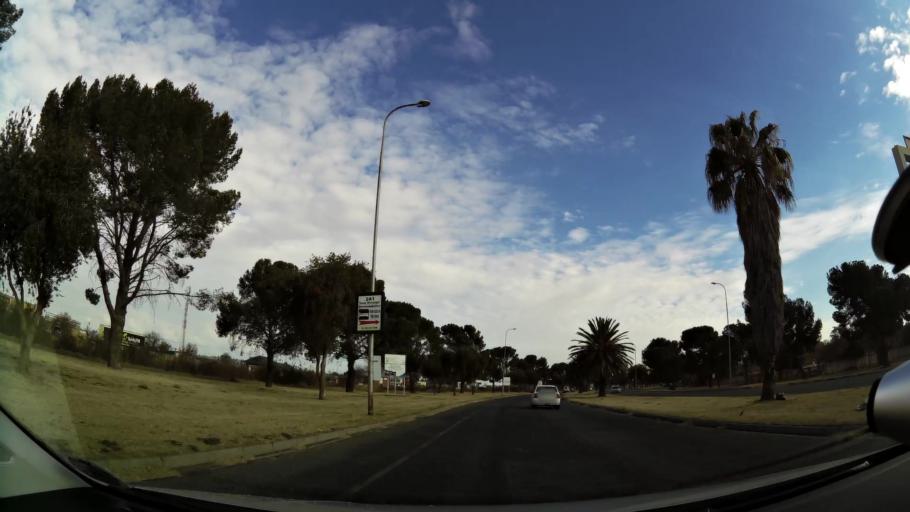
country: ZA
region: Orange Free State
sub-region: Lejweleputswa District Municipality
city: Welkom
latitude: -27.9832
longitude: 26.7603
